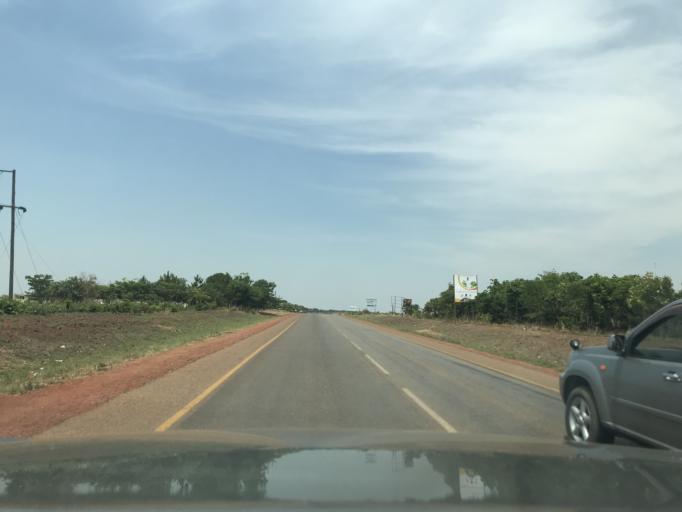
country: ZM
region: Northern
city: Kasama
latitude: -10.2178
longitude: 31.1436
